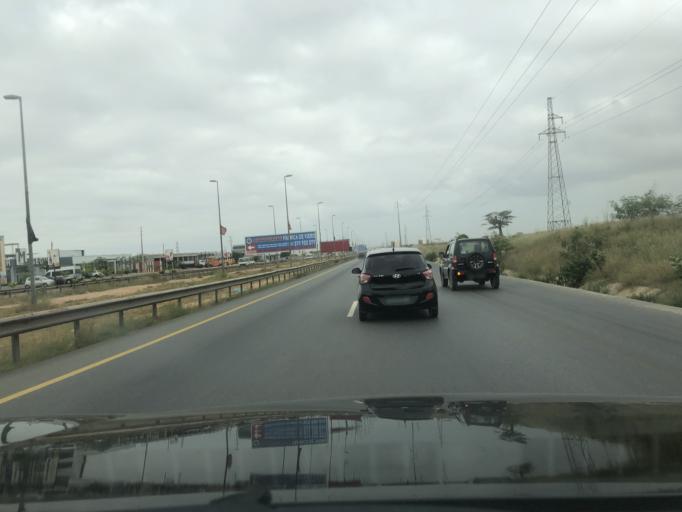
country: AO
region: Luanda
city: Luanda
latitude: -8.9735
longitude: 13.2311
